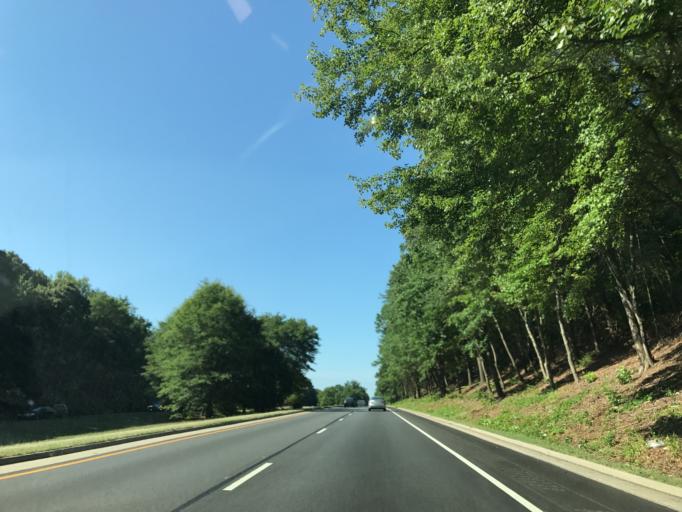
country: US
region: Maryland
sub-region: Prince George's County
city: Greenbelt
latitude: 39.0158
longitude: -76.8601
